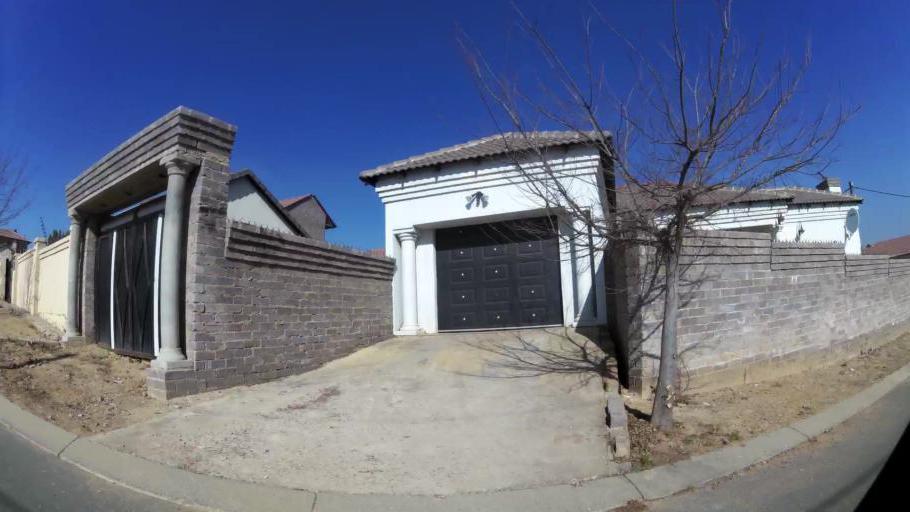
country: ZA
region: Gauteng
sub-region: West Rand District Municipality
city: Muldersdriseloop
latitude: -26.0347
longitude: 27.9206
